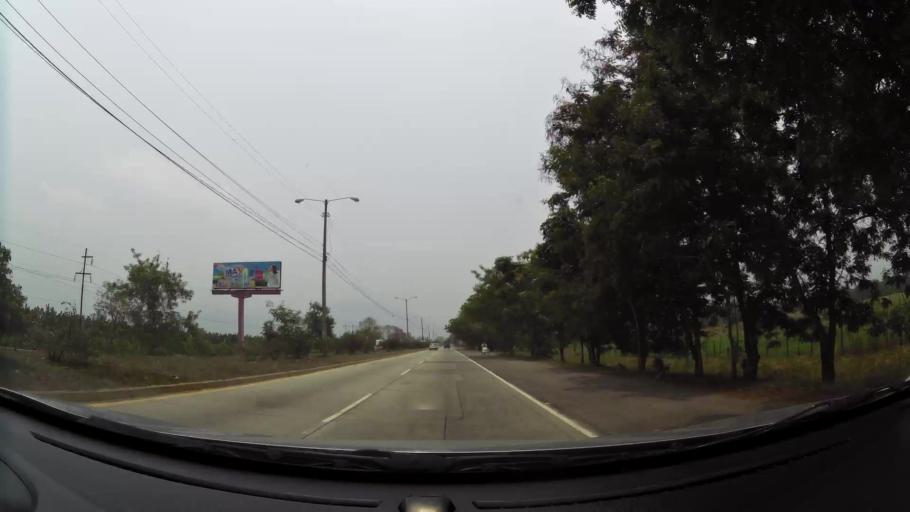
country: HN
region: Yoro
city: El Progreso
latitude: 15.4063
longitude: -87.8279
